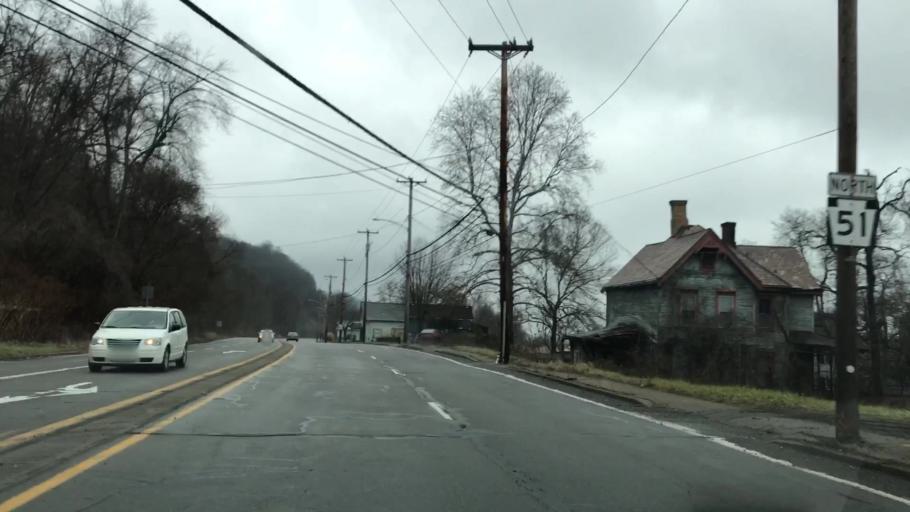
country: US
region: Pennsylvania
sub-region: Beaver County
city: Ambridge
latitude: 40.5771
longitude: -80.2363
